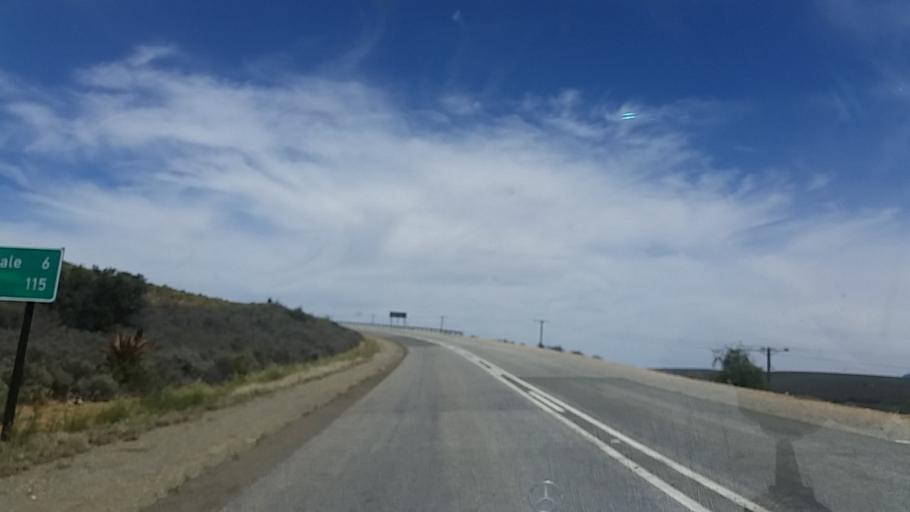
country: ZA
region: Western Cape
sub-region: Eden District Municipality
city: Knysna
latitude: -33.6286
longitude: 23.1292
